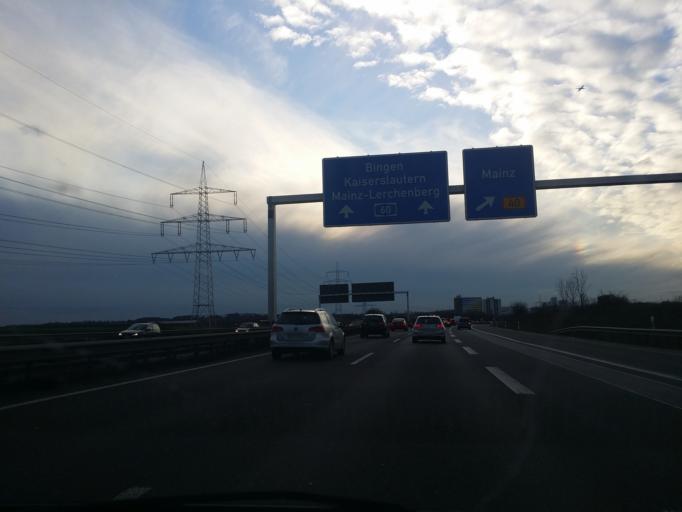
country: DE
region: Rheinland-Pfalz
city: Mainz
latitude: 49.9651
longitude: 8.2480
